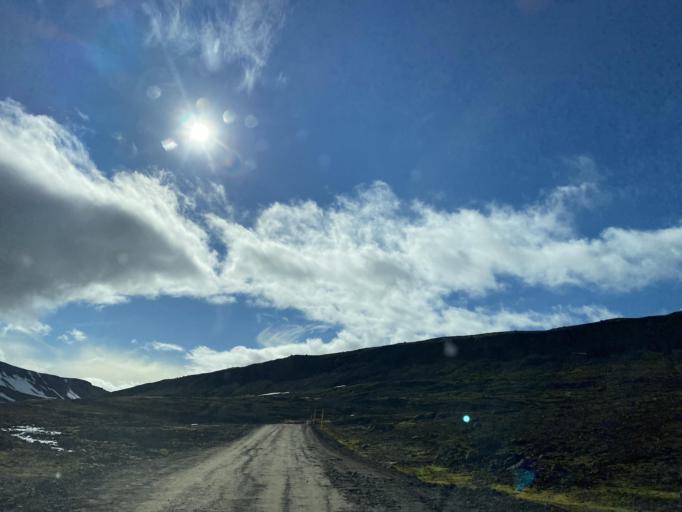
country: IS
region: East
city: Eskifjoerdur
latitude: 65.1678
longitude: -14.1341
